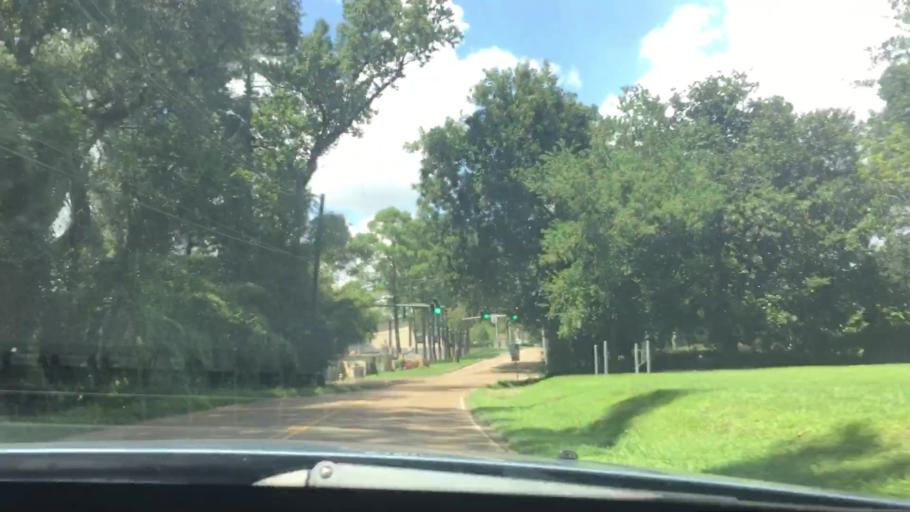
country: US
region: Louisiana
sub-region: East Baton Rouge Parish
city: Gardere
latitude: 30.3654
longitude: -91.1178
